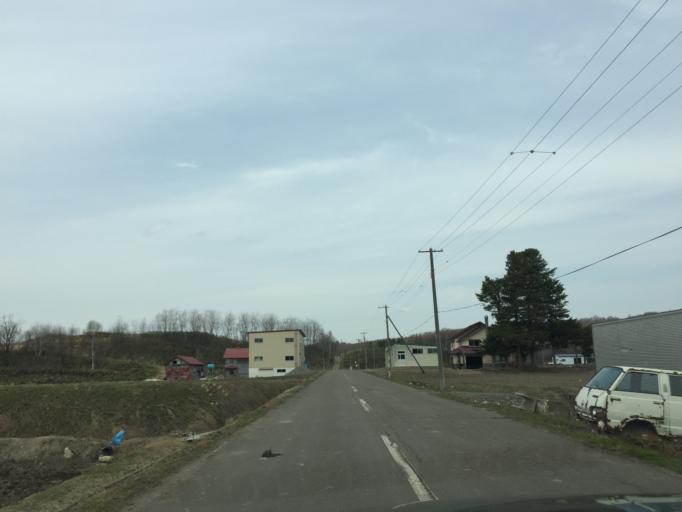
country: JP
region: Hokkaido
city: Ashibetsu
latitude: 43.6175
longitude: 142.2151
